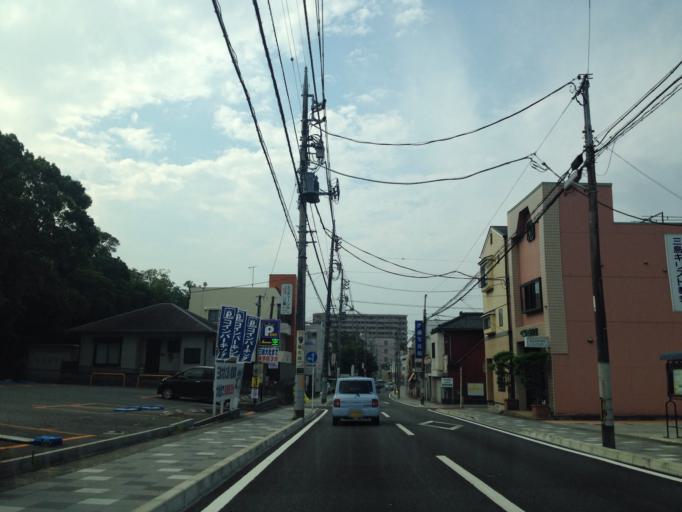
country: JP
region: Shizuoka
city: Mishima
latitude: 35.1226
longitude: 138.9178
